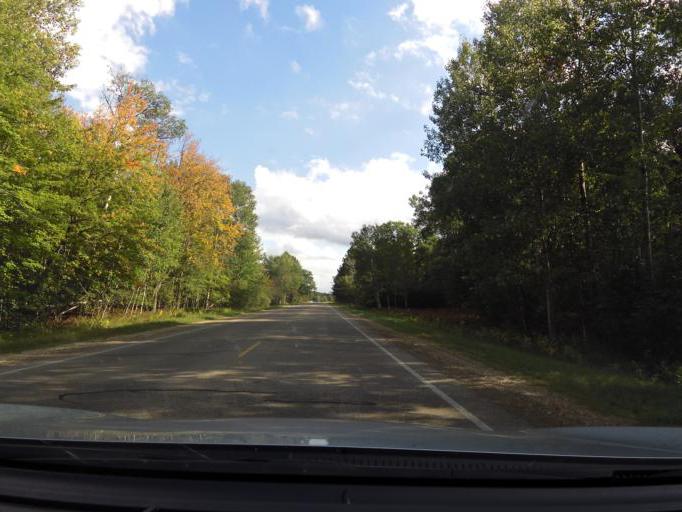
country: US
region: Michigan
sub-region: Roscommon County
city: Saint Helen
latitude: 44.3864
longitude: -84.4285
